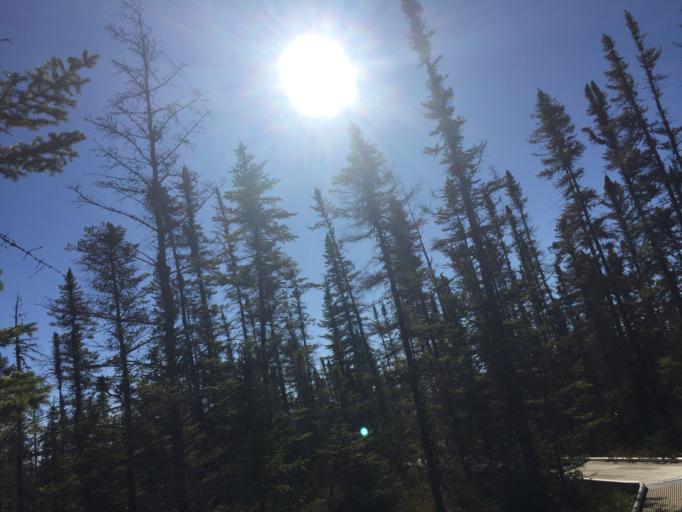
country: US
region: Minnesota
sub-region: Lake of the Woods County
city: Baudette
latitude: 48.2938
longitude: -94.5668
